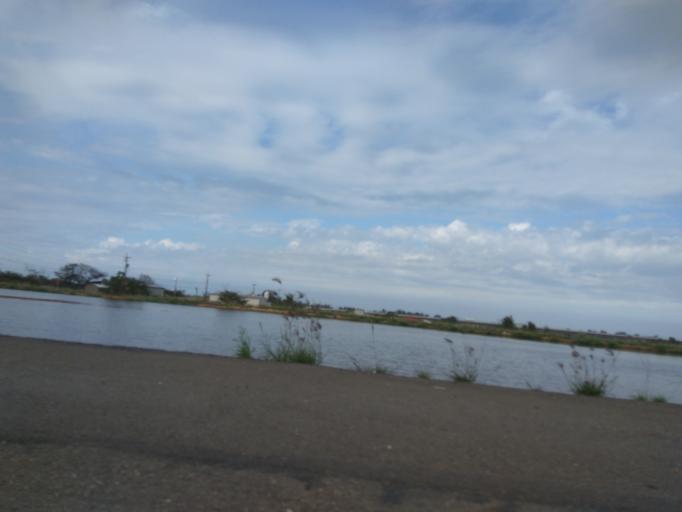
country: TW
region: Taiwan
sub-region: Hsinchu
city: Zhubei
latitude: 24.9517
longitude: 121.0104
